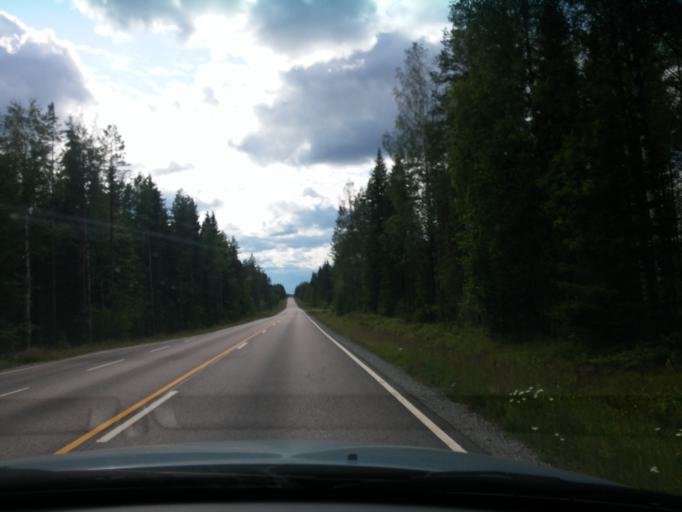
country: FI
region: Central Finland
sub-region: Saarijaervi-Viitasaari
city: Pylkoenmaeki
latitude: 62.6082
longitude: 24.6766
